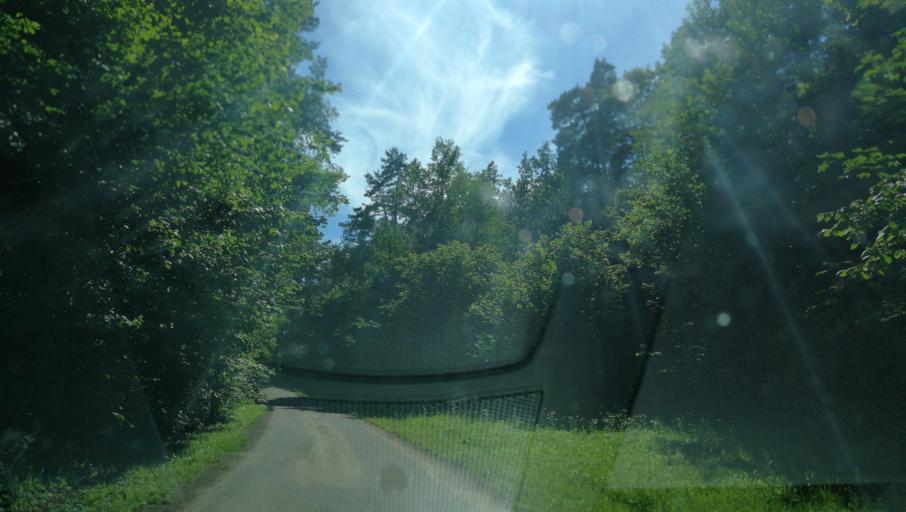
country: LV
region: Cesvaine
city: Cesvaine
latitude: 56.9715
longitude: 26.3192
